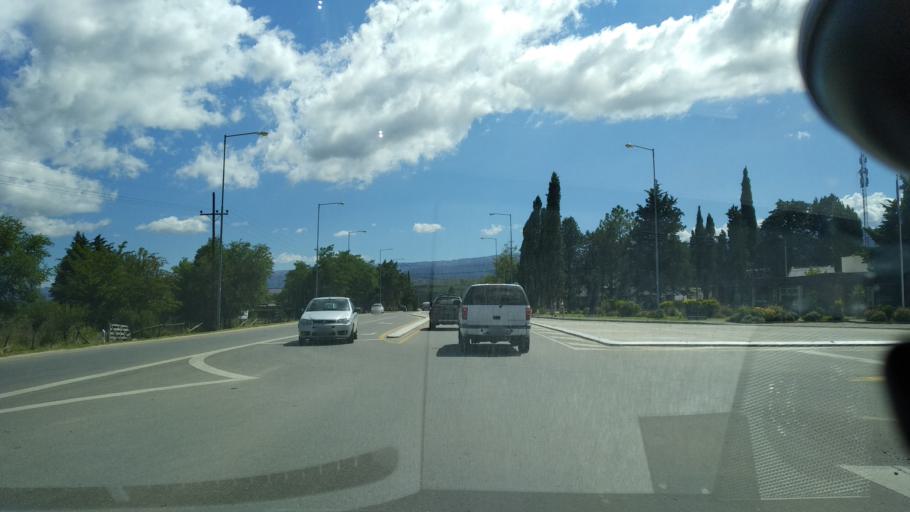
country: AR
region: Cordoba
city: Mina Clavero
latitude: -31.7930
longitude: -65.0015
